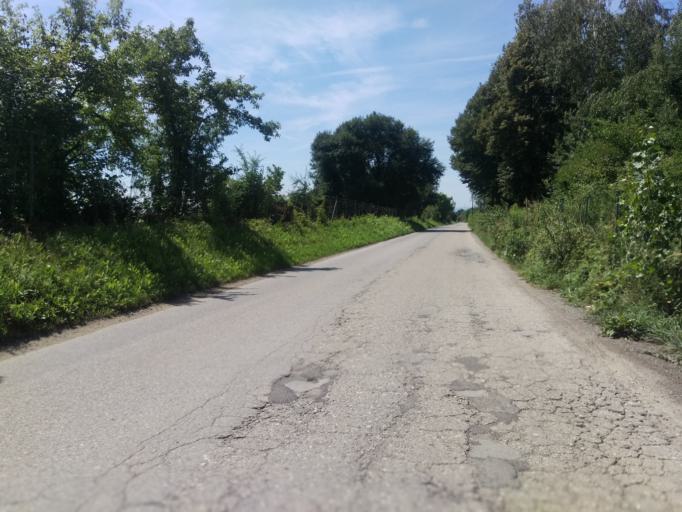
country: AT
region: Styria
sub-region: Politischer Bezirk Graz-Umgebung
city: Seiersberg
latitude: 46.9956
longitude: 15.4244
